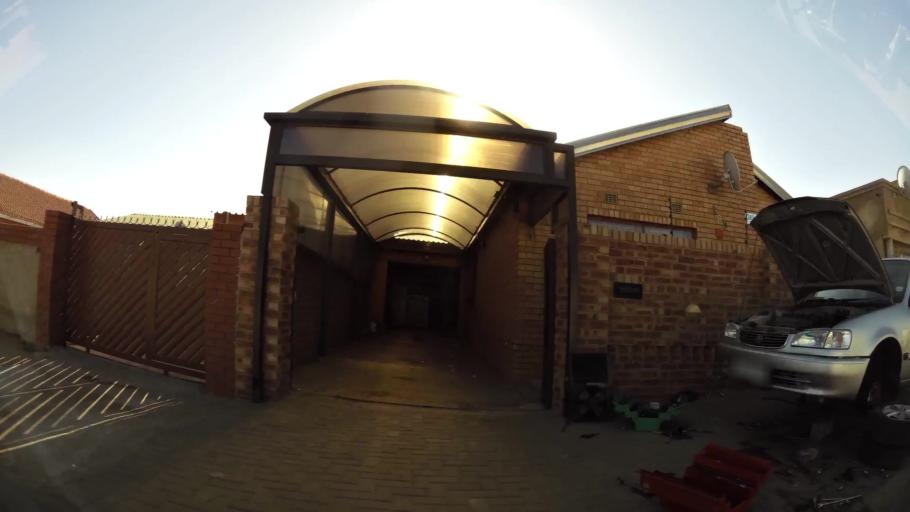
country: ZA
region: Gauteng
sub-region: Ekurhuleni Metropolitan Municipality
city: Tembisa
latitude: -26.0269
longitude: 28.2194
